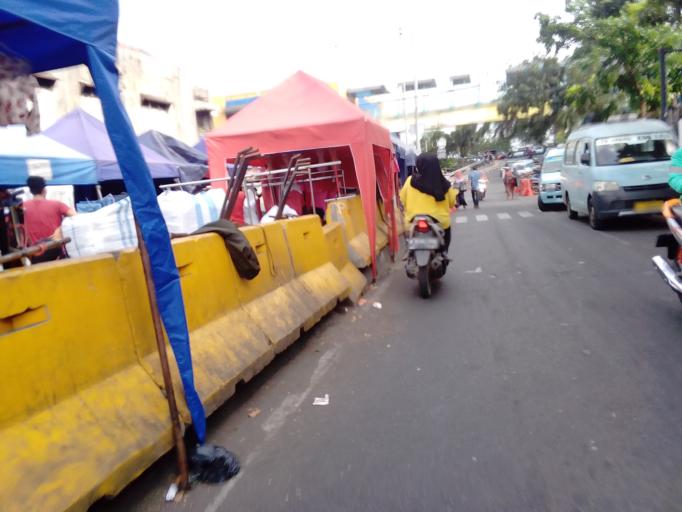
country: ID
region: Jakarta Raya
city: Jakarta
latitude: -6.1882
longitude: 106.8114
